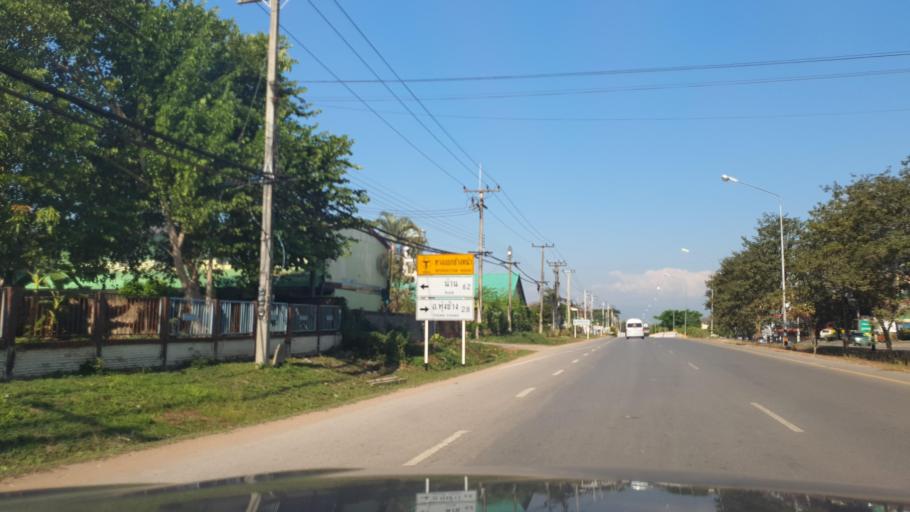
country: TH
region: Nan
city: Pua
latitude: 19.1724
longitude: 100.9192
